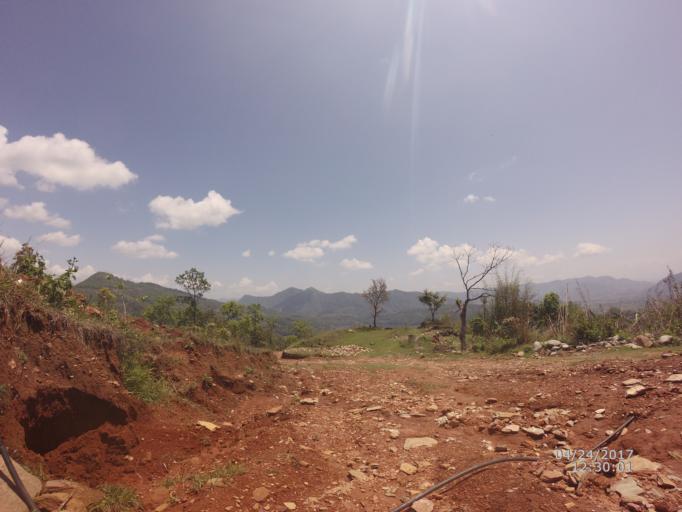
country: NP
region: Western Region
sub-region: Gandaki Zone
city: Pokhara
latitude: 28.1896
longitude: 84.0867
